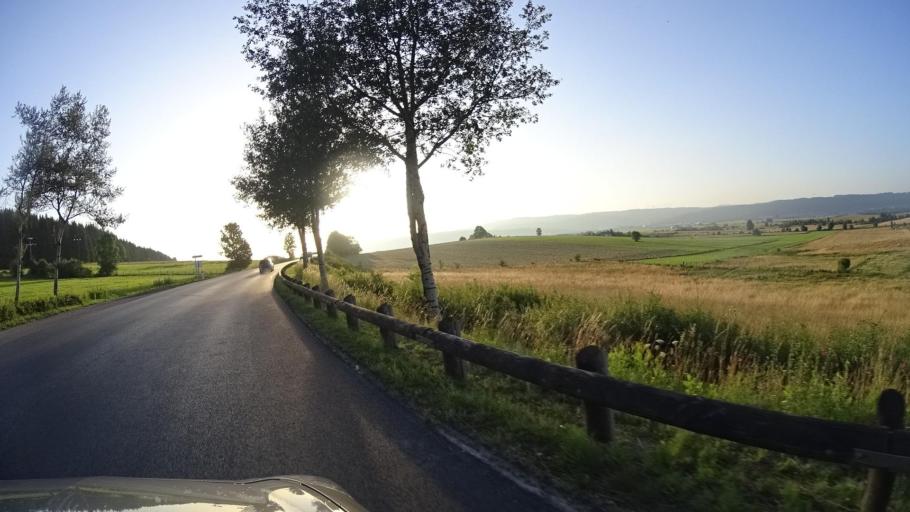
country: FR
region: Franche-Comte
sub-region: Departement du Doubs
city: Doubs
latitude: 46.9159
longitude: 6.2863
